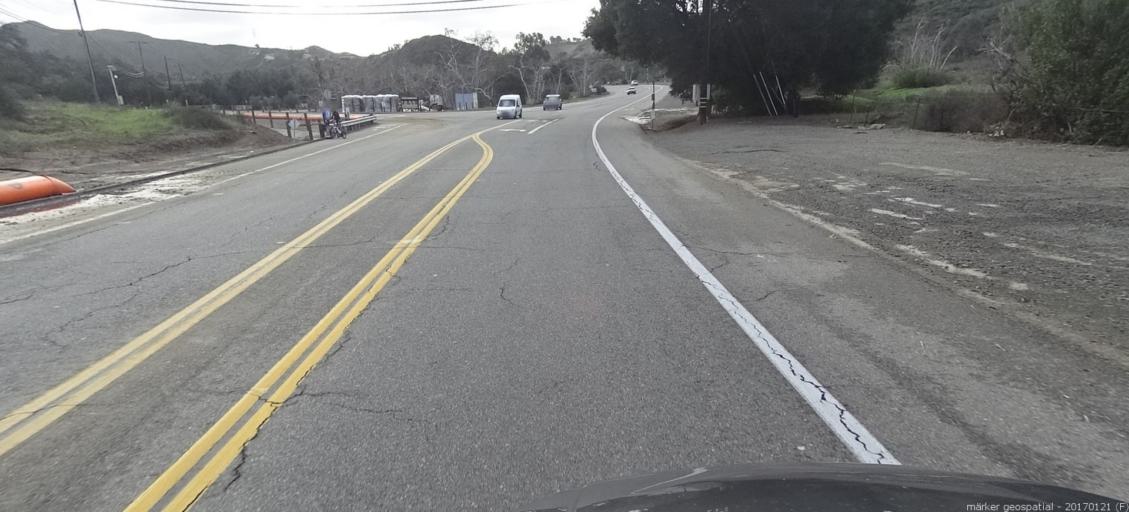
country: US
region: California
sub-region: Orange County
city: Foothill Ranch
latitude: 33.7180
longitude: -117.6465
